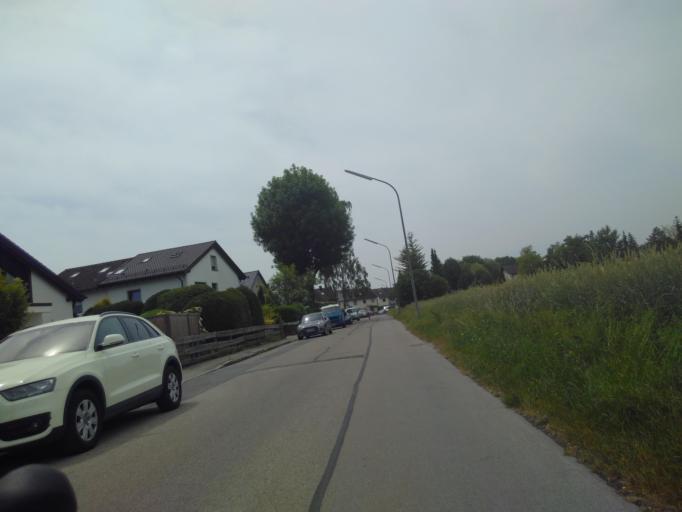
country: DE
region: Bavaria
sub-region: Upper Bavaria
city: Eichenau
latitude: 48.1605
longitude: 11.3155
